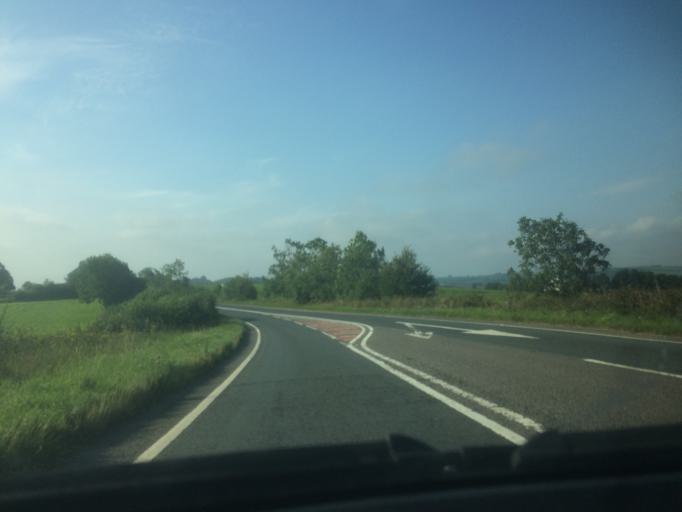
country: GB
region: England
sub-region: Cornwall
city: Pillaton
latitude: 50.4511
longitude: -4.2558
